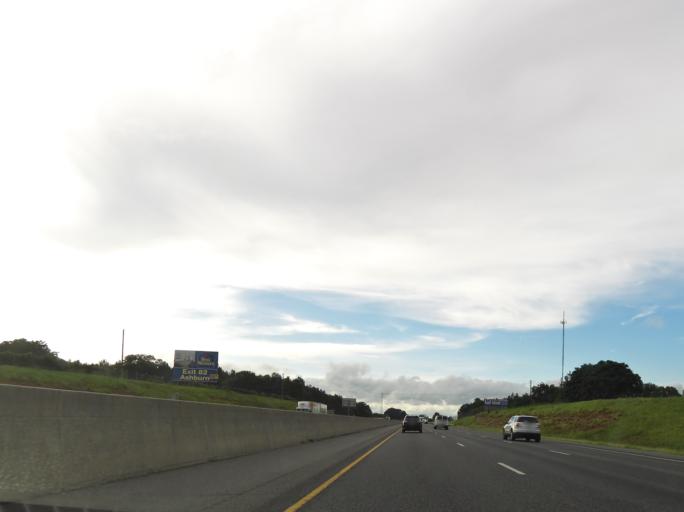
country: US
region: Georgia
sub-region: Tift County
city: Tifton
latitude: 31.5630
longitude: -83.5421
